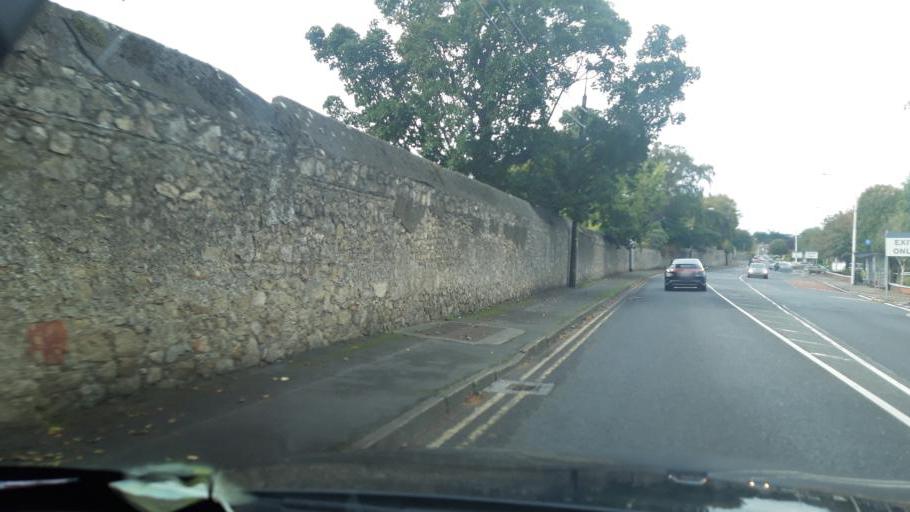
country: IE
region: Leinster
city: Cabinteely
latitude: 53.2654
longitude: -6.1608
